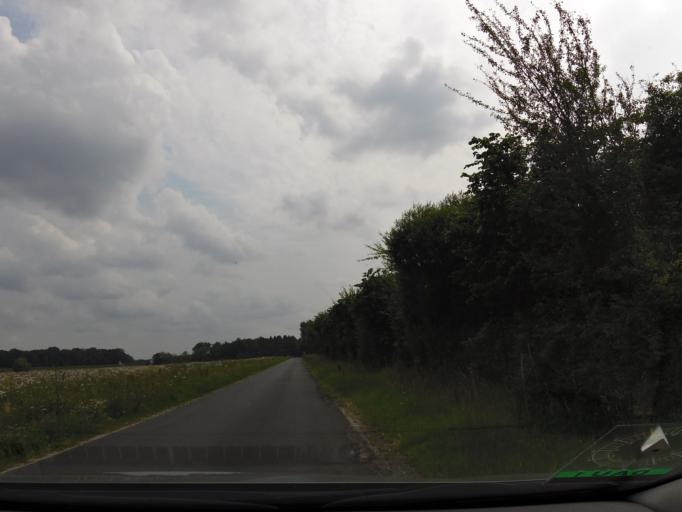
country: DK
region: South Denmark
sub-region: Odense Kommune
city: Neder Holluf
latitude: 55.3829
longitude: 10.4730
